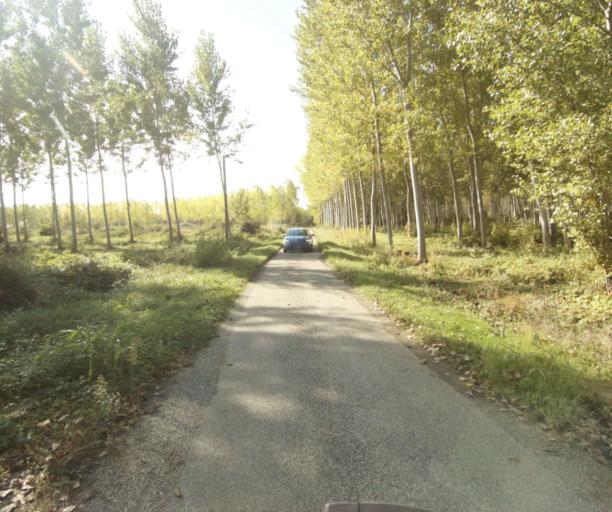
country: FR
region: Midi-Pyrenees
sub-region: Departement du Tarn-et-Garonne
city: Finhan
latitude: 43.9045
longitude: 1.2211
